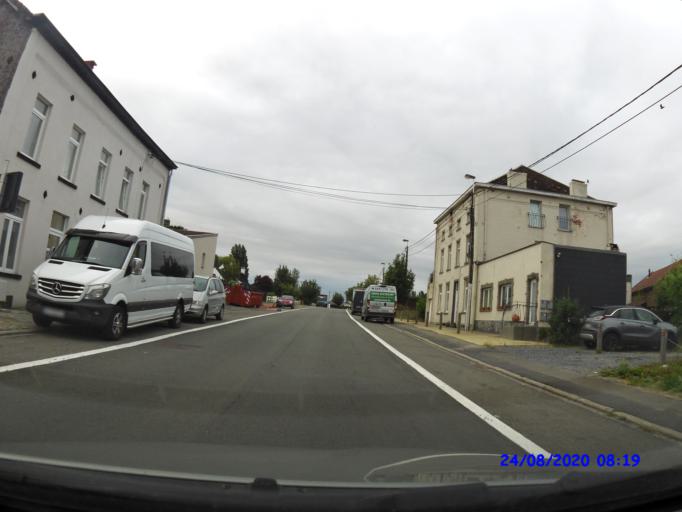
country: BE
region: Wallonia
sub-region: Province du Brabant Wallon
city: Genappe
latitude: 50.5990
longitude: 4.4555
